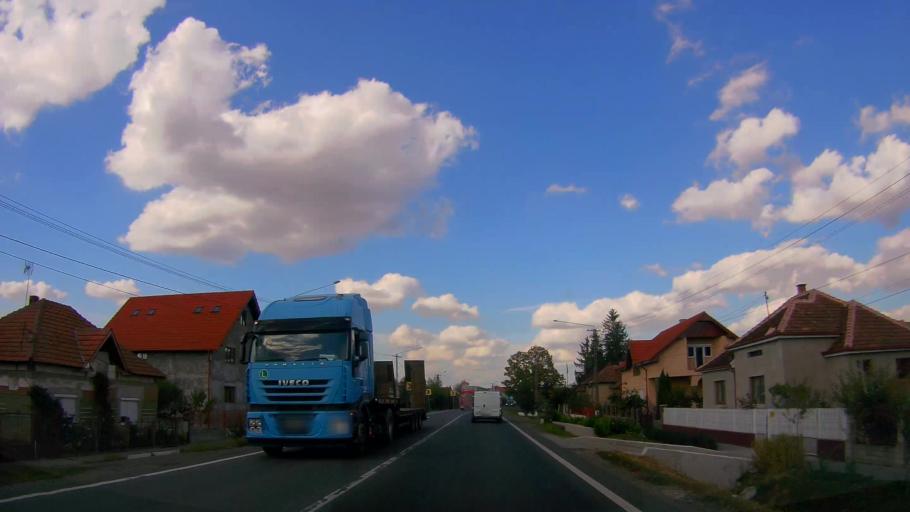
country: RO
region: Satu Mare
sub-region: Comuna Botiz
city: Botiz
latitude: 47.8313
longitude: 22.9536
